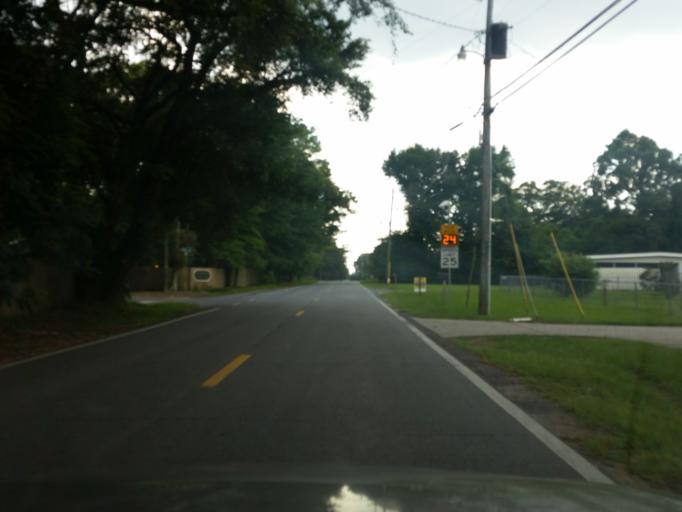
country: US
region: Florida
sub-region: Escambia County
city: Ferry Pass
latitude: 30.4938
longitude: -87.2121
